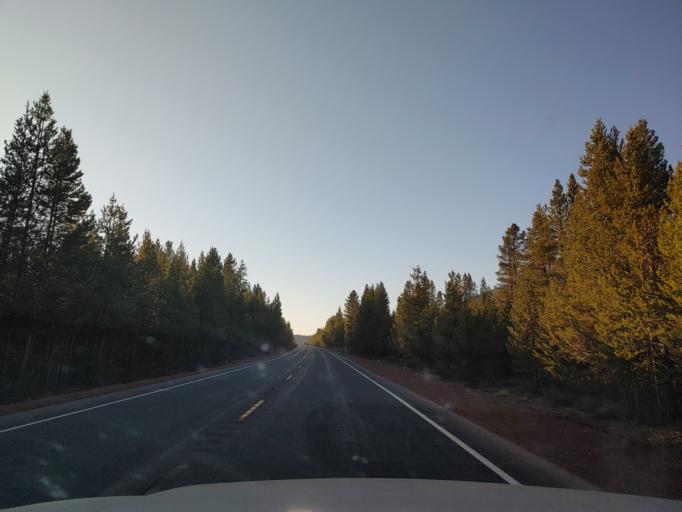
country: US
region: Oregon
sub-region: Deschutes County
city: La Pine
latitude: 43.4204
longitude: -121.8409
